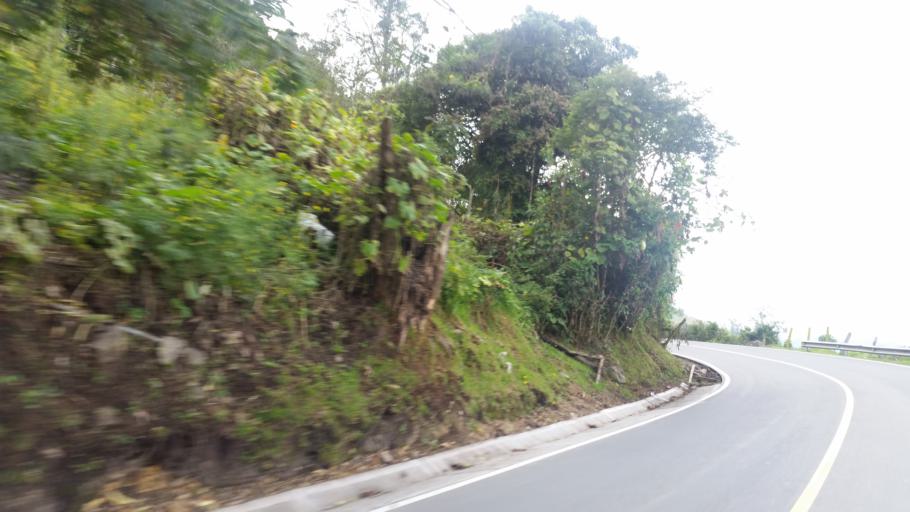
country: CO
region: Cundinamarca
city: Choachi
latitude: 4.5517
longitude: -73.9323
